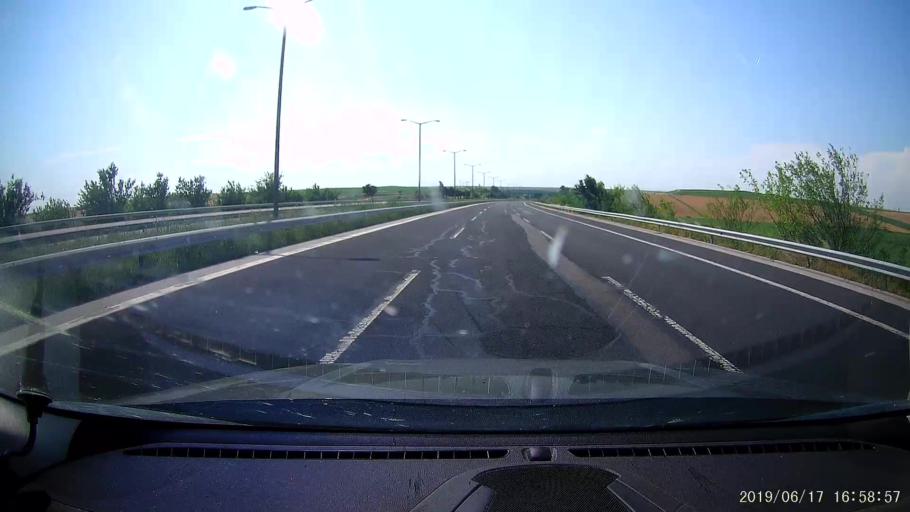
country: TR
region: Edirne
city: Haskoy
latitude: 41.6116
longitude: 26.8730
